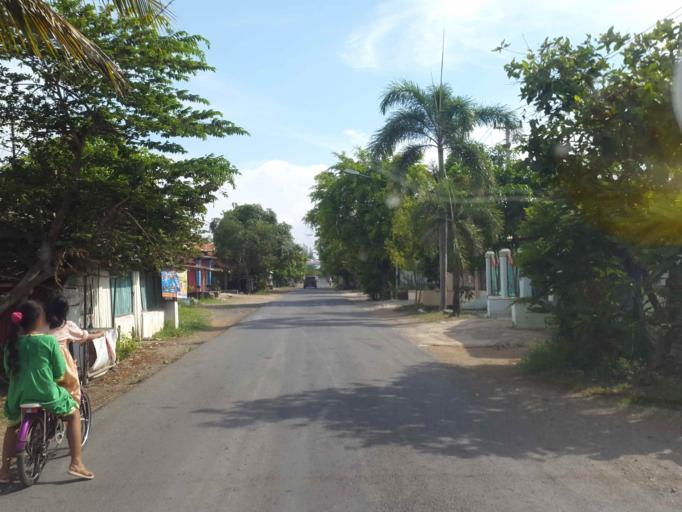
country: ID
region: Central Java
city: Pemalang
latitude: -6.8838
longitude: 109.3273
